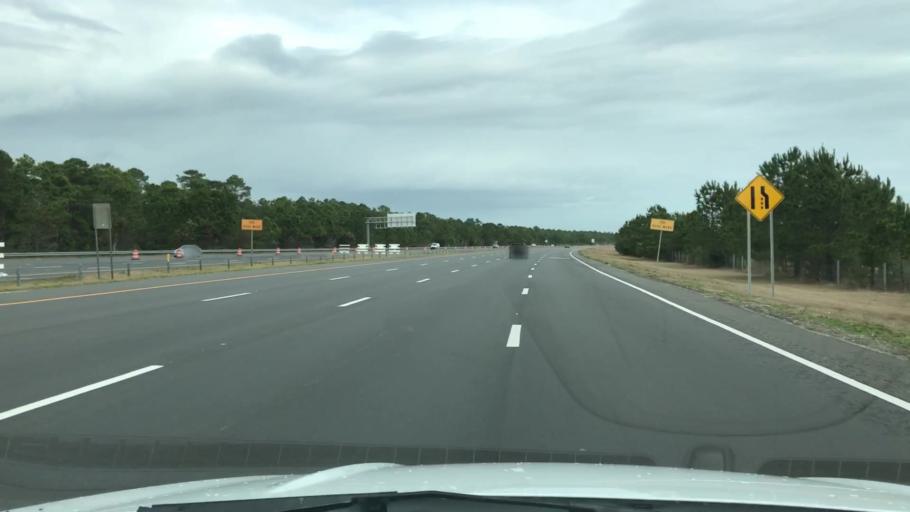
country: US
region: South Carolina
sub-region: Horry County
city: Socastee
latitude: 33.7084
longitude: -79.0098
